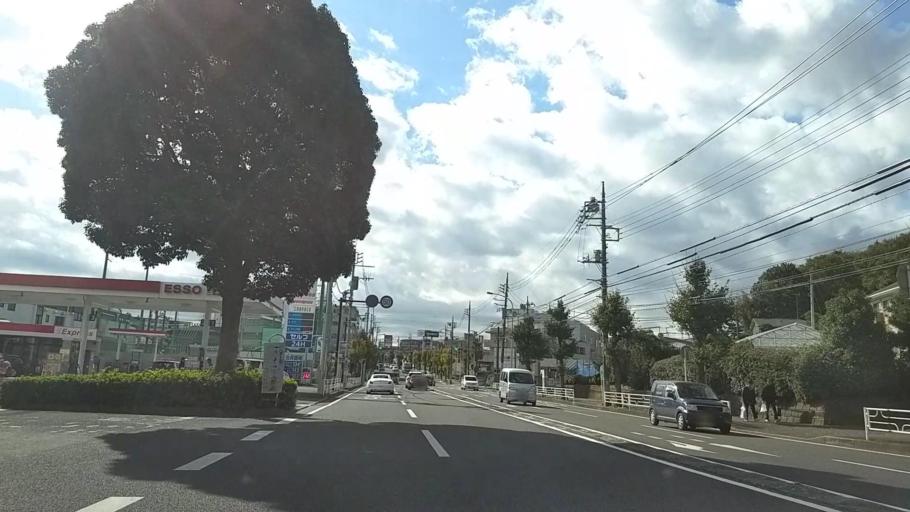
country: JP
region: Kanagawa
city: Yokohama
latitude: 35.4902
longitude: 139.6066
